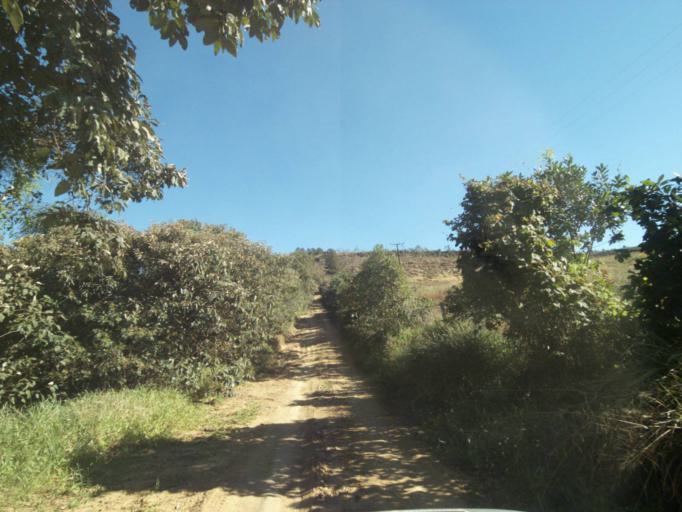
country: BR
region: Parana
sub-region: Tibagi
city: Tibagi
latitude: -24.5766
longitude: -50.4789
